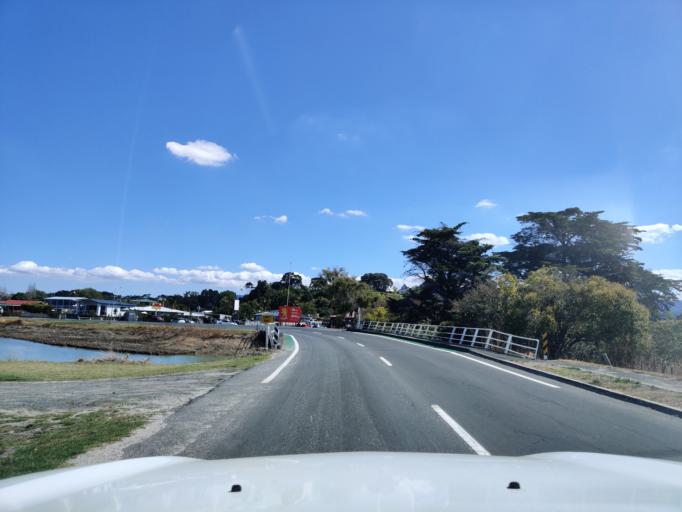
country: NZ
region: Waikato
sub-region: Thames-Coromandel District
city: Thames
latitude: -37.1092
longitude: 175.2980
